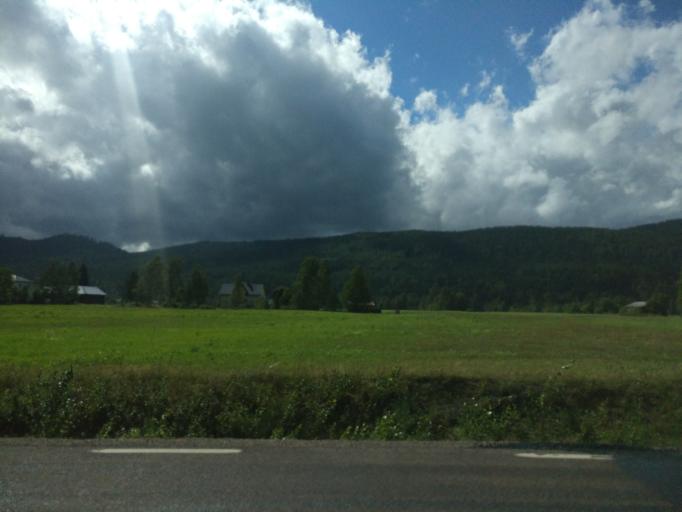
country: SE
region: Vaermland
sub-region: Hagfors Kommun
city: Ekshaerad
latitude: 60.3547
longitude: 13.3294
